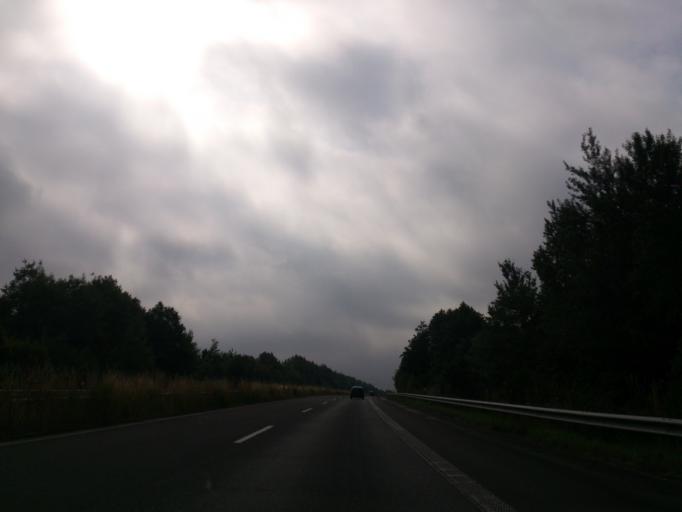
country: DE
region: Schleswig-Holstein
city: Arkebek
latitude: 54.1570
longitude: 9.2268
